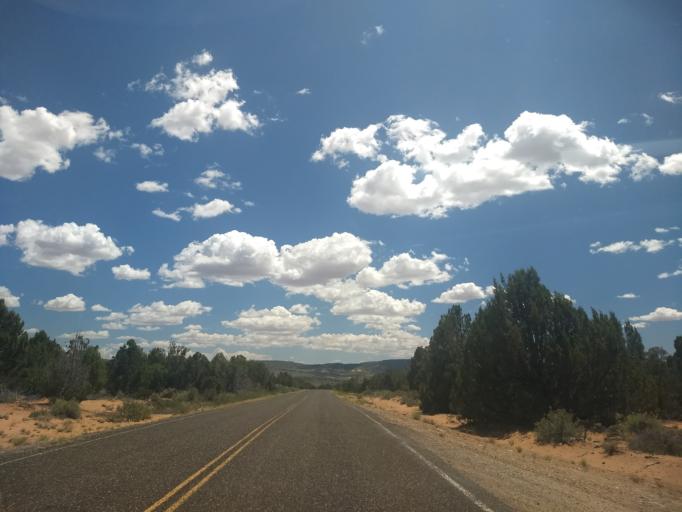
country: US
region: Utah
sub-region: Kane County
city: Kanab
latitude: 37.1842
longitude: -112.6545
